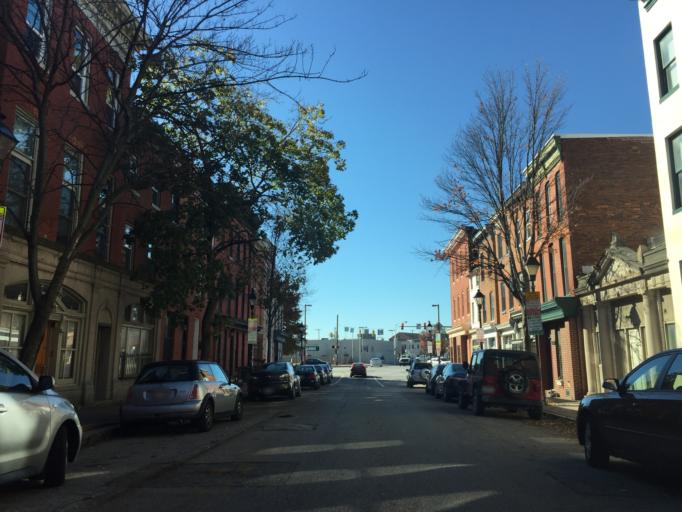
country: US
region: Maryland
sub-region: City of Baltimore
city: Baltimore
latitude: 39.2840
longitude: -76.6253
